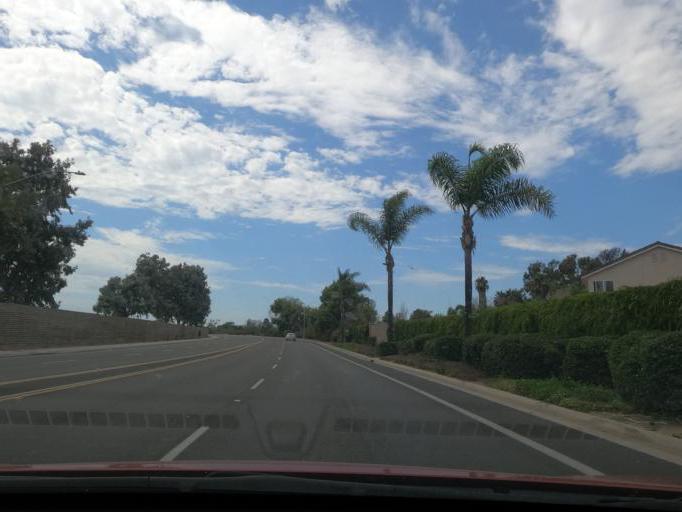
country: US
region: California
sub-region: San Diego County
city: Imperial Beach
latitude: 32.5509
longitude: -117.0556
